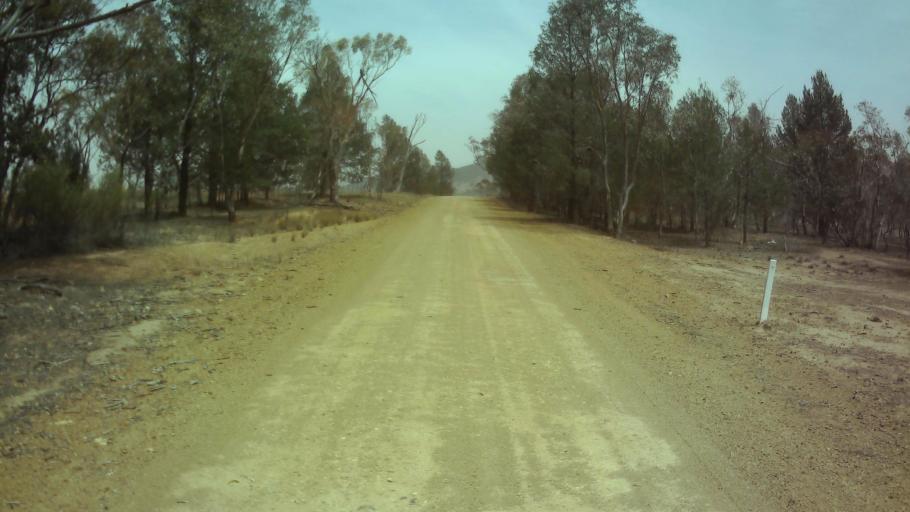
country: AU
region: New South Wales
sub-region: Weddin
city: Grenfell
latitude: -33.7450
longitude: 147.9725
